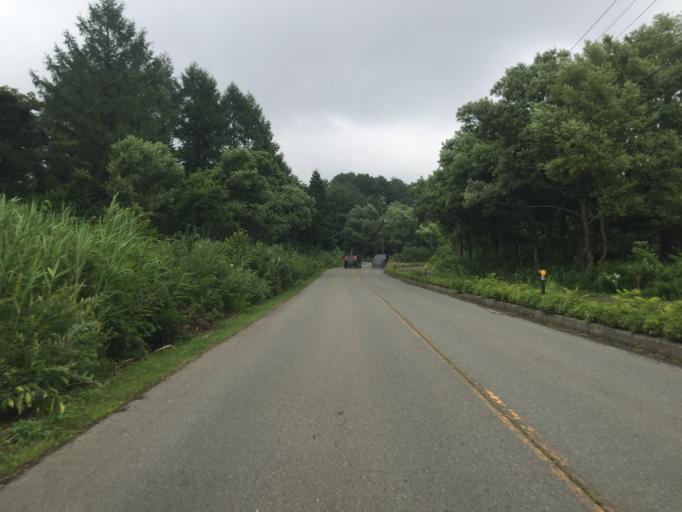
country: JP
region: Fukushima
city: Inawashiro
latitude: 37.6715
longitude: 140.0769
